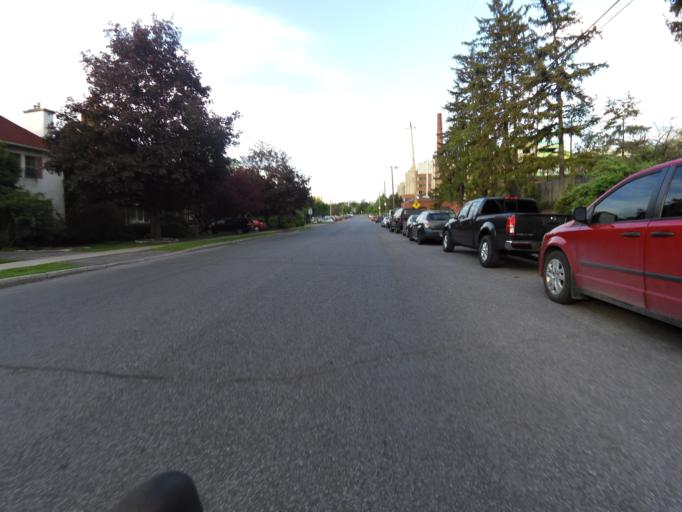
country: CA
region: Ontario
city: Ottawa
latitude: 45.3937
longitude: -75.7236
